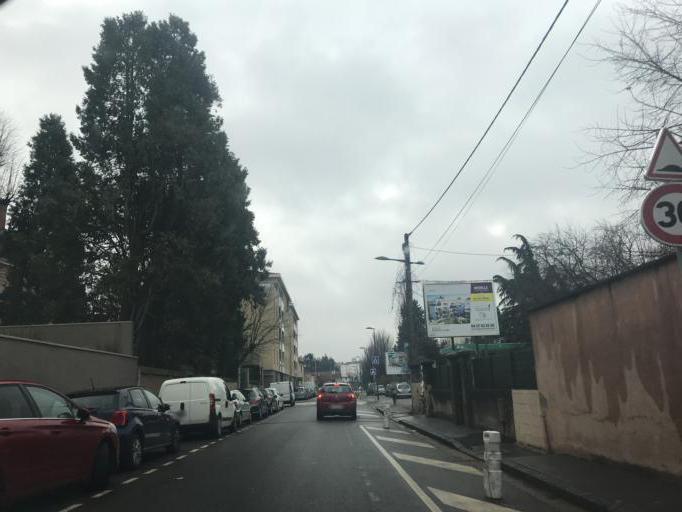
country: FR
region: Rhone-Alpes
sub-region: Departement du Rhone
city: Albigny-sur-Saone
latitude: 45.8732
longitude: 4.8393
